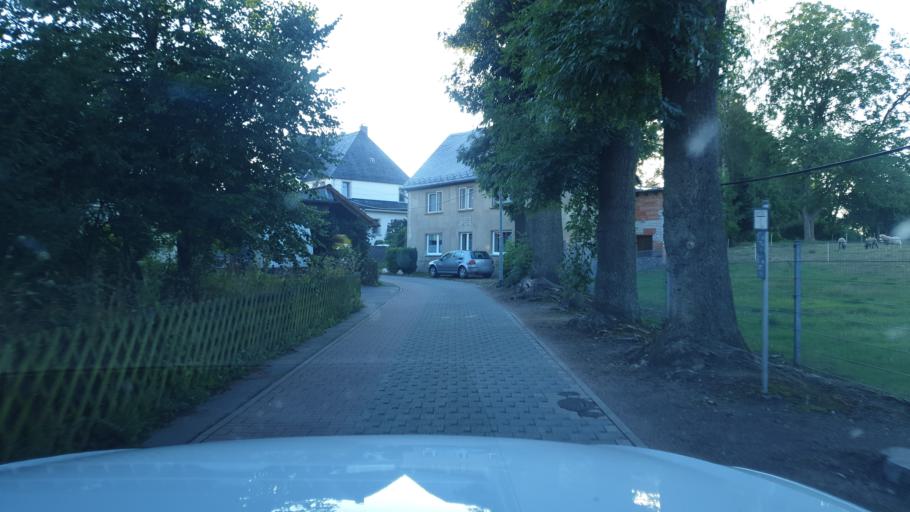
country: DE
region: Saxony
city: Altmittweida
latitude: 50.9647
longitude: 12.9510
